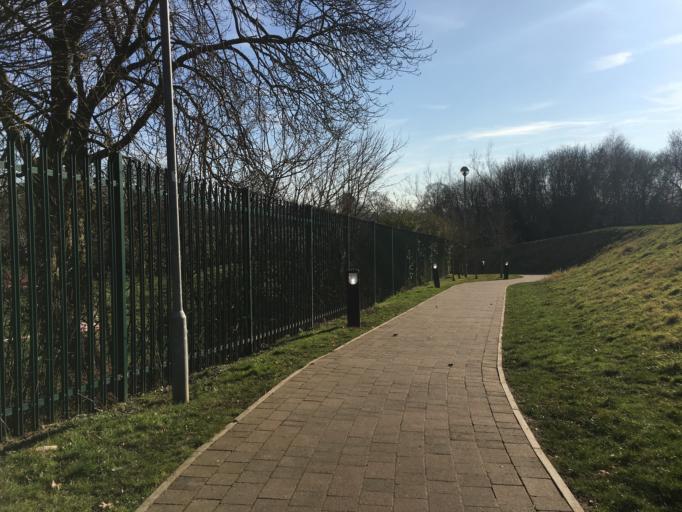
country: GB
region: England
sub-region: Warwickshire
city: Rugby
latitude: 52.3656
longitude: -1.2542
